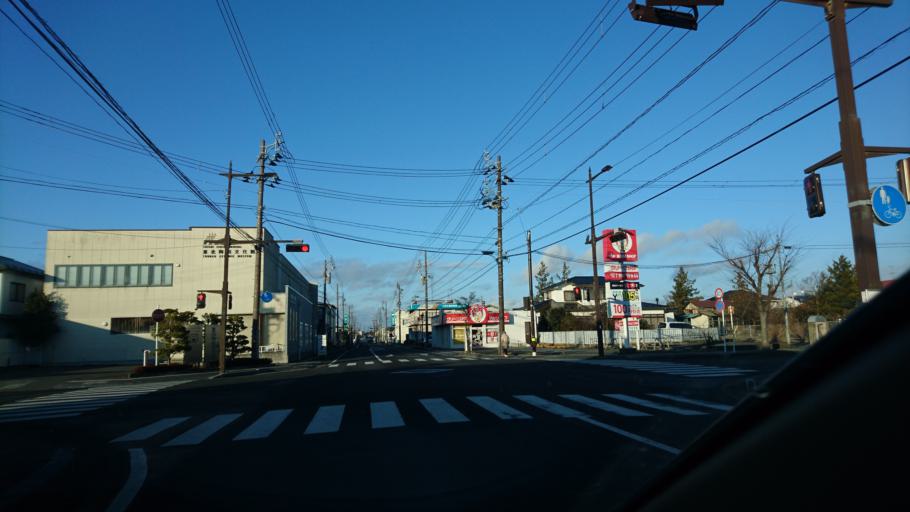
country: JP
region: Miyagi
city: Furukawa
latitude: 38.5675
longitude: 140.8594
